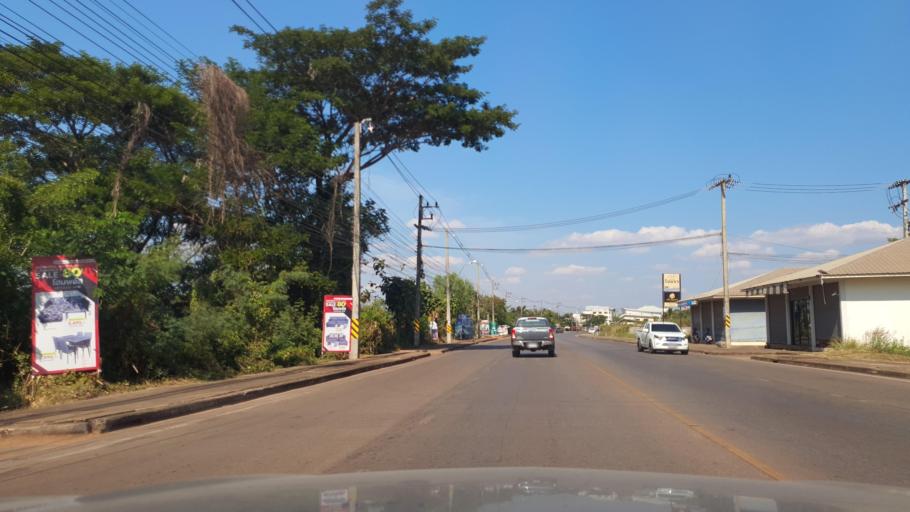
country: TH
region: Sakon Nakhon
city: Sakon Nakhon
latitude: 17.1696
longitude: 104.1254
